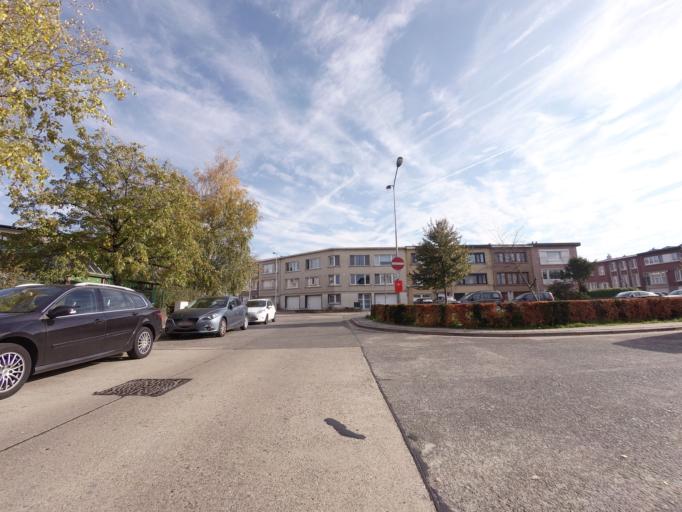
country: BE
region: Flanders
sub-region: Provincie Antwerpen
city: Borsbeek
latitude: 51.2271
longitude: 4.4769
